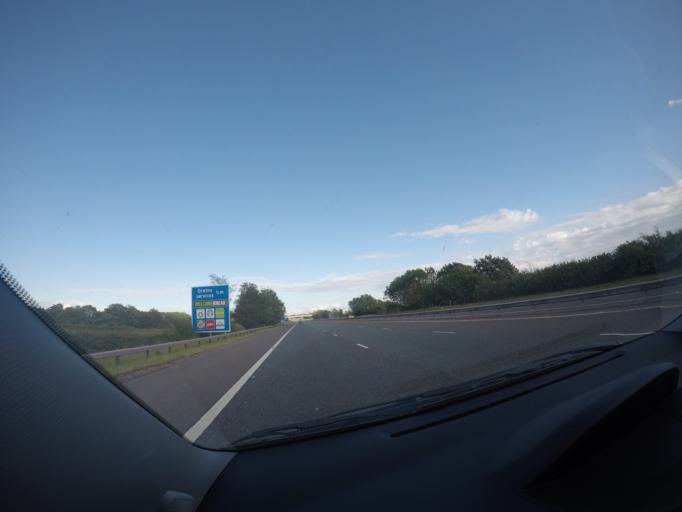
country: GB
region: Scotland
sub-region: Dumfries and Galloway
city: Gretna
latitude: 55.0154
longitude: -3.1082
